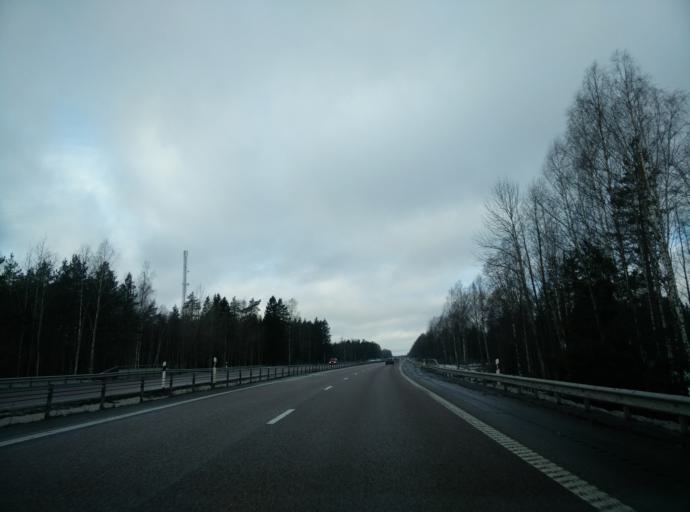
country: SE
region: Gaevleborg
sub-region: Gavle Kommun
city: Valbo
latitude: 60.6280
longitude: 16.9605
